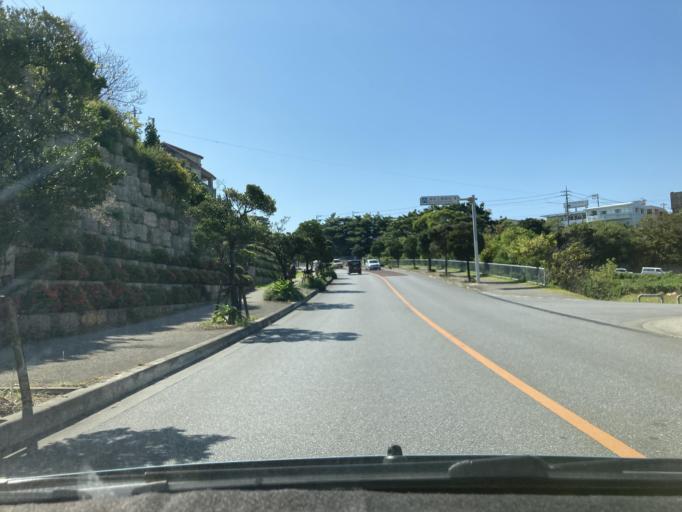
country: JP
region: Okinawa
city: Ginowan
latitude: 26.2435
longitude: 127.7258
